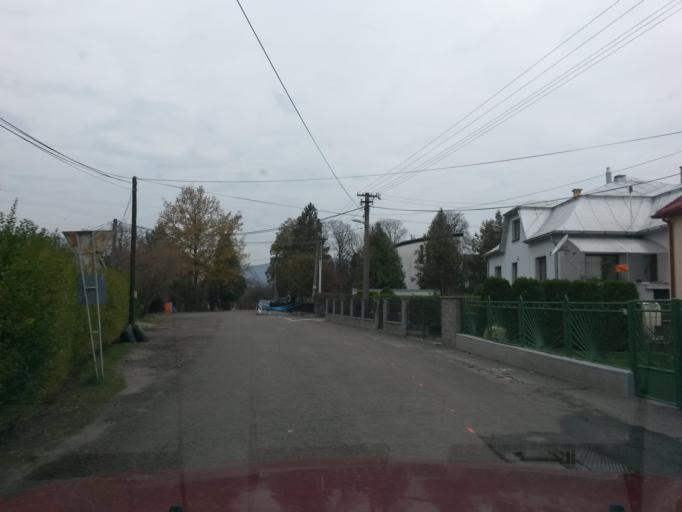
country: SK
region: Kosicky
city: Secovce
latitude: 48.7054
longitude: 21.6497
